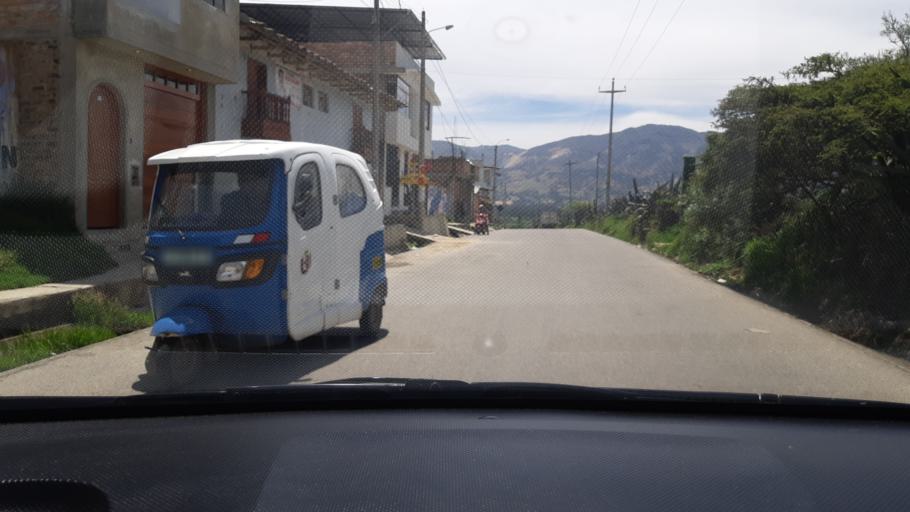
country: PE
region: Cajamarca
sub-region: Provincia de Cajamarca
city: Llacanora
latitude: -7.1731
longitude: -78.4580
